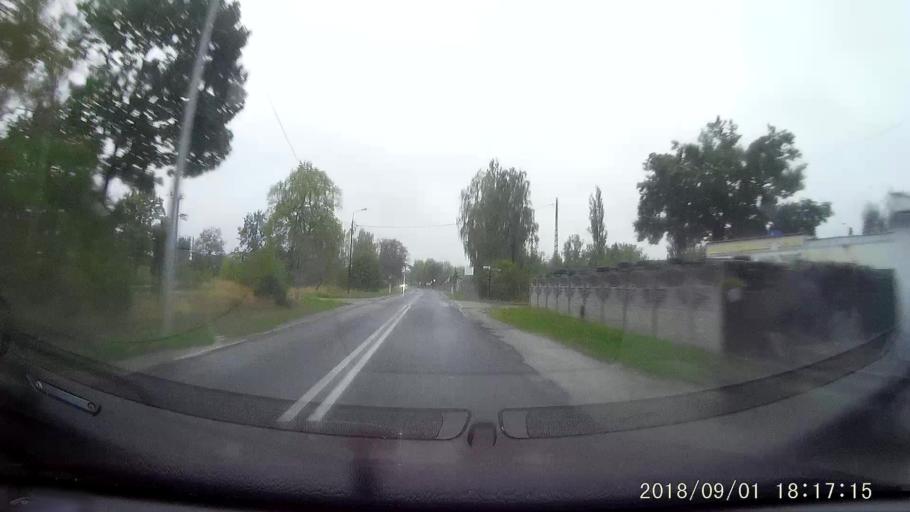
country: PL
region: Lower Silesian Voivodeship
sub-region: Powiat zgorzelecki
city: Piensk
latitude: 51.2639
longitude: 15.0491
